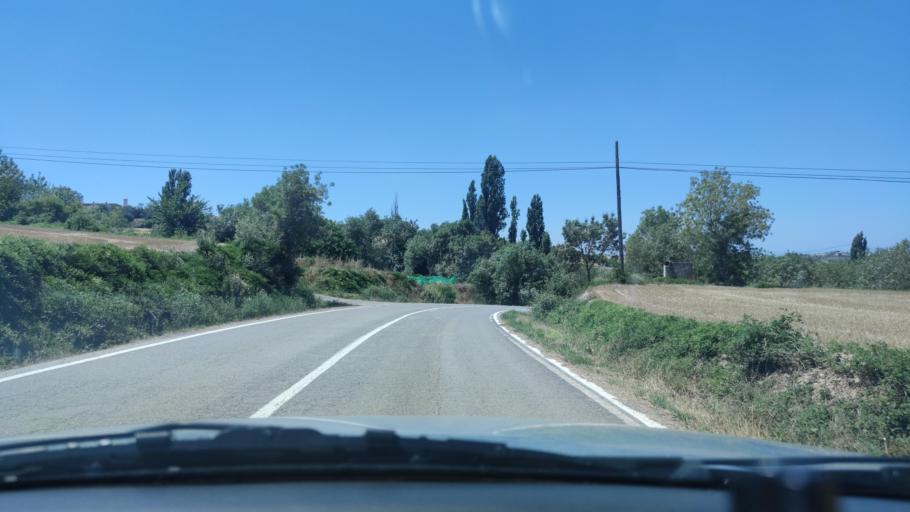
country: ES
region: Catalonia
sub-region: Provincia de Lleida
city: Ivorra
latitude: 41.7699
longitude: 1.3920
